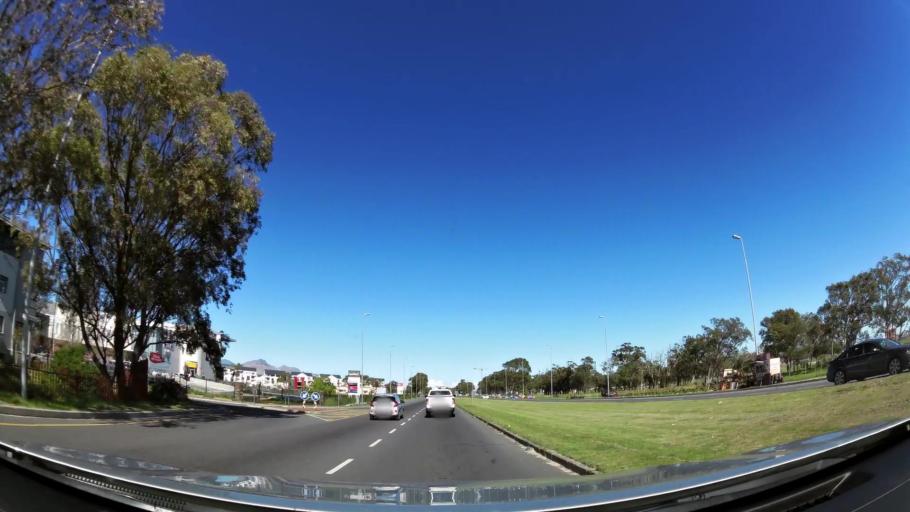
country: ZA
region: Western Cape
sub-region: Cape Winelands District Municipality
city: Stellenbosch
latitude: -34.0871
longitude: 18.8200
